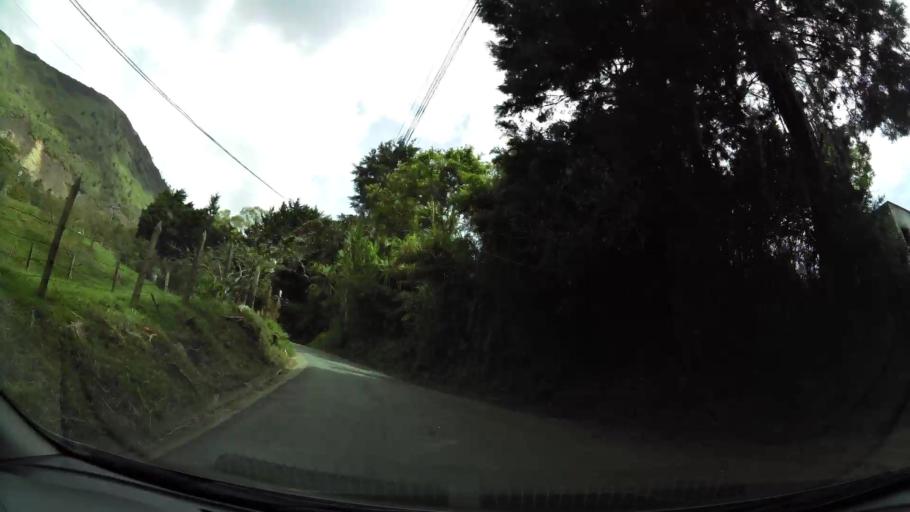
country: CO
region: Antioquia
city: Municipio de Copacabana
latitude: 6.3225
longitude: -75.4944
